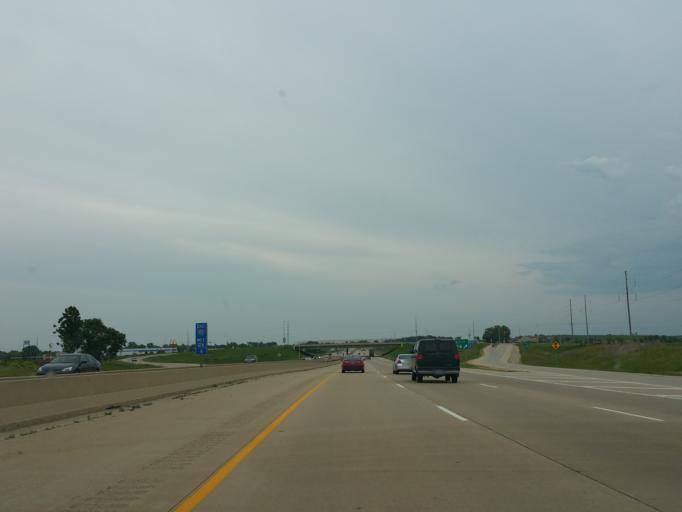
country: US
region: Wisconsin
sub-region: Dane County
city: De Forest
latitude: 43.2542
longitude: -89.3801
